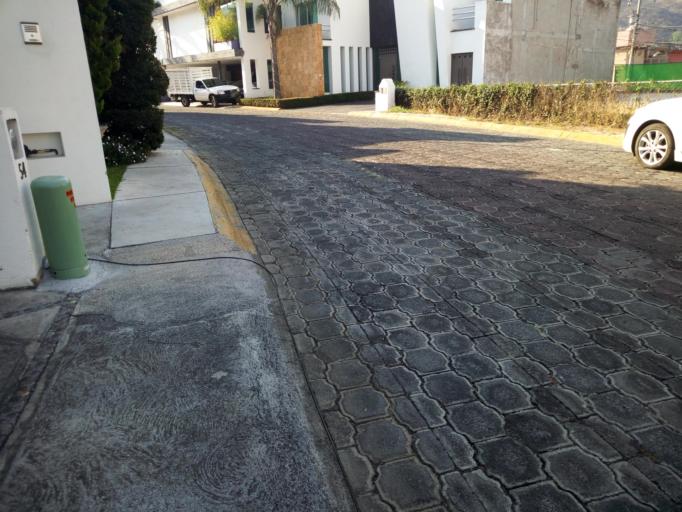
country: MX
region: Michoacan
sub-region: Morelia
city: Puerto de Buenavista (Lazaro Cardenas)
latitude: 19.6911
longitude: -101.1477
